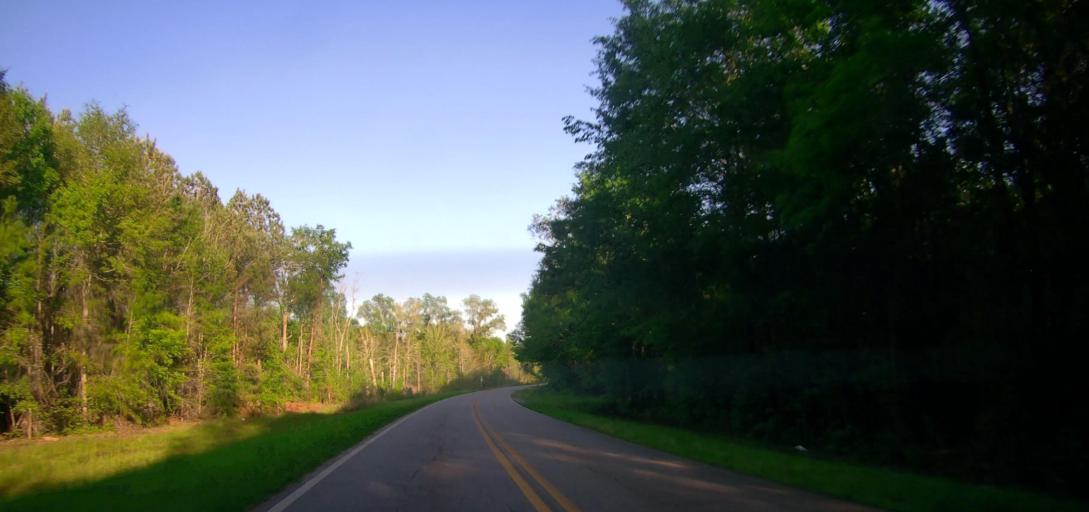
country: US
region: Georgia
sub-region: Macon County
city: Oglethorpe
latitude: 32.3046
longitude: -84.1060
